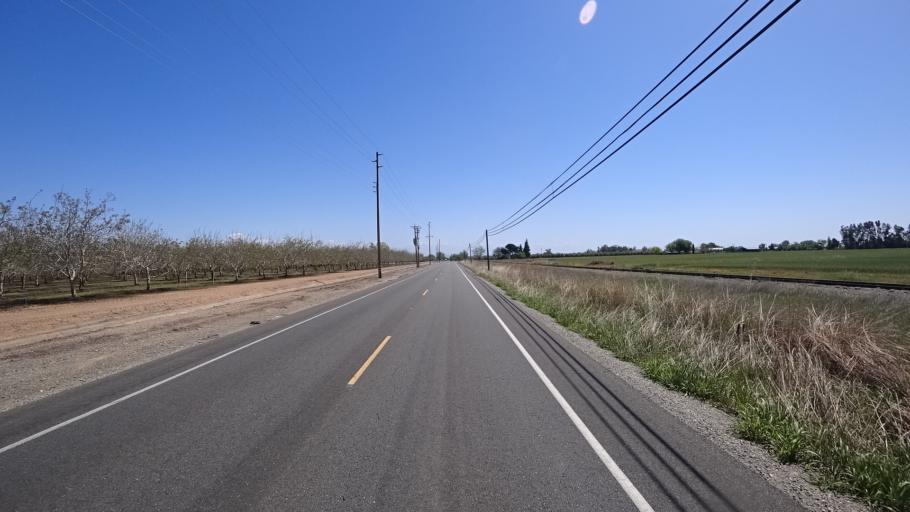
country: US
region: California
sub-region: Glenn County
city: Orland
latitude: 39.7688
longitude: -122.1728
